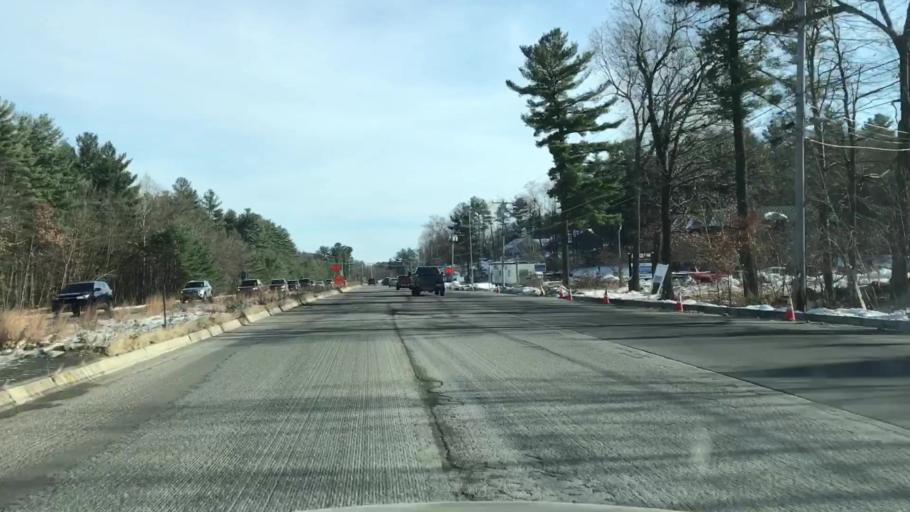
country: US
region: New Hampshire
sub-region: Hillsborough County
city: Milford
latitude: 42.8242
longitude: -71.6131
